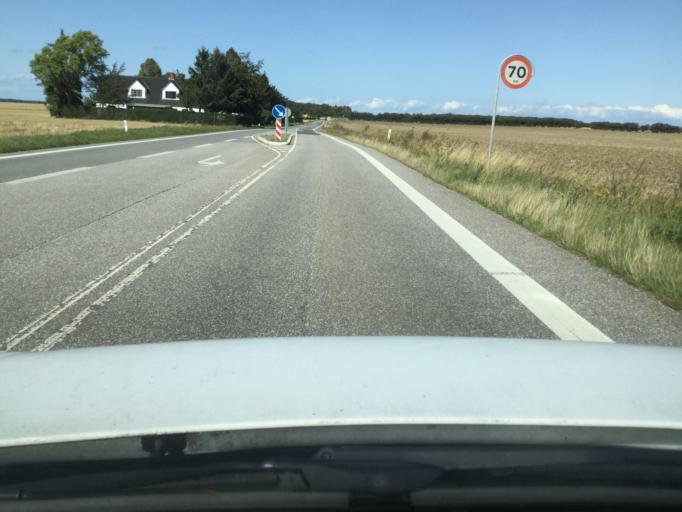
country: DK
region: Zealand
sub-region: Lolland Kommune
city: Rodby
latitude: 54.7128
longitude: 11.3823
